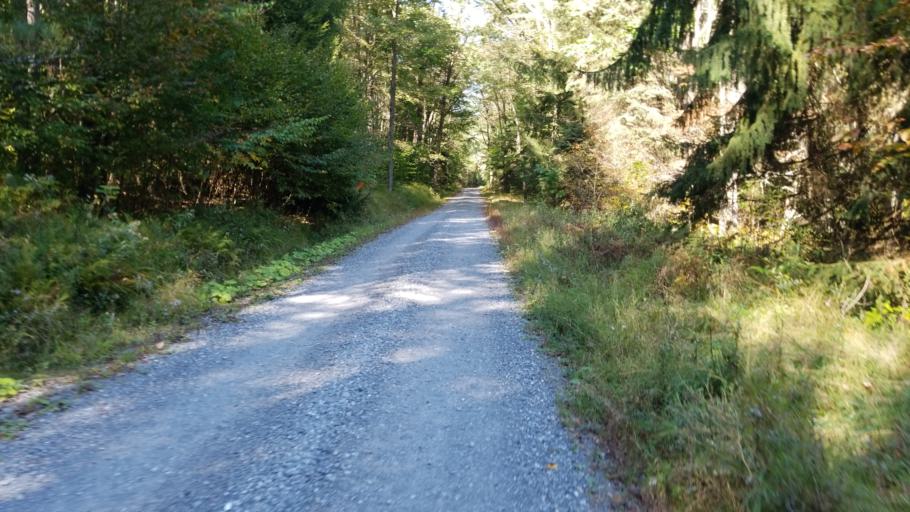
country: US
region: Pennsylvania
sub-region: Clearfield County
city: Clearfield
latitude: 41.1874
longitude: -78.5147
